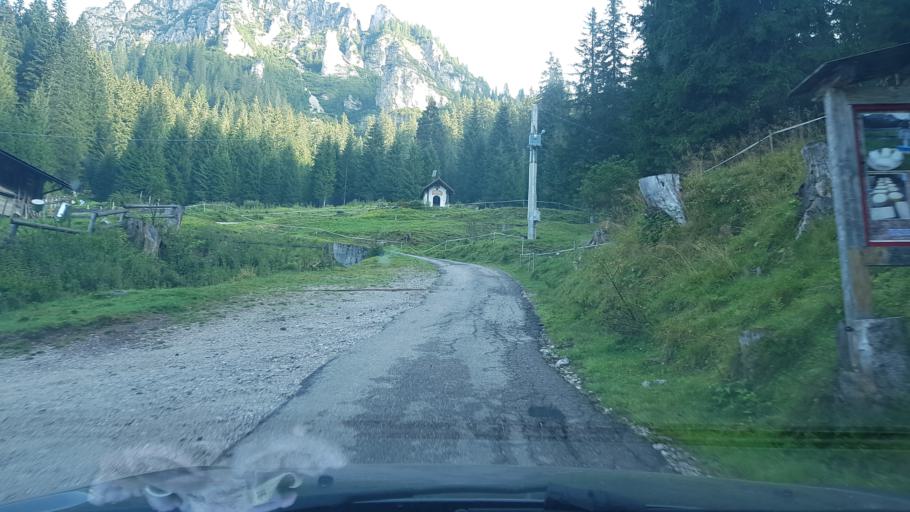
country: IT
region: Veneto
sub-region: Provincia di Belluno
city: San Pietro di Cadore
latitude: 46.6019
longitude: 12.5882
